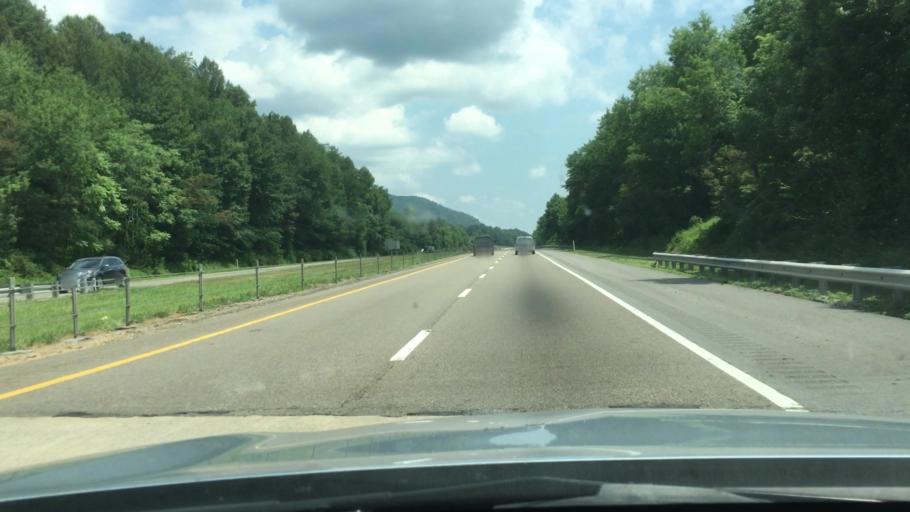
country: US
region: Tennessee
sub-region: Unicoi County
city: Unicoi
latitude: 36.2185
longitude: -82.3439
